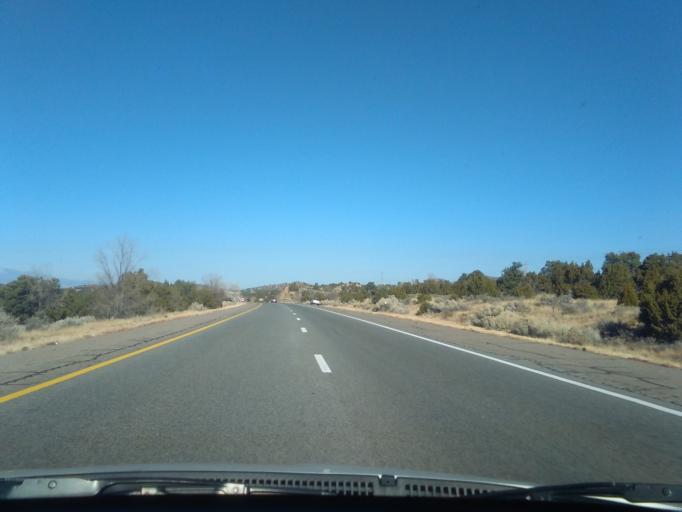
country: US
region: New Mexico
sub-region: Santa Fe County
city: Eldorado at Santa Fe
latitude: 35.5875
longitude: -105.9016
